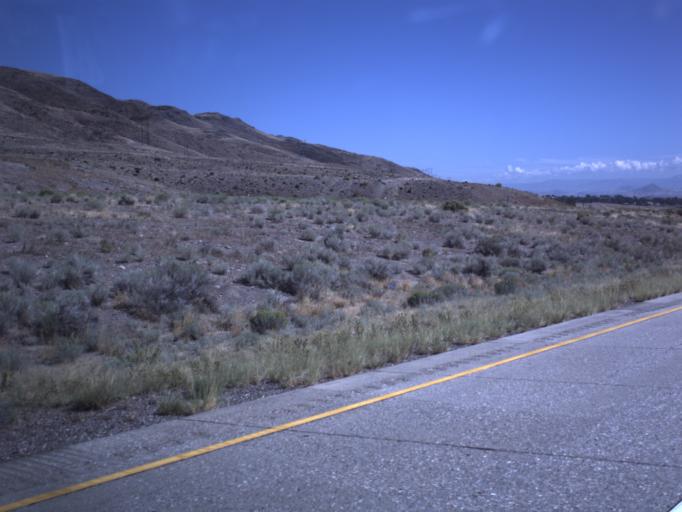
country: US
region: Utah
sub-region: Sevier County
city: Monroe
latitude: 38.6593
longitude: -112.1821
